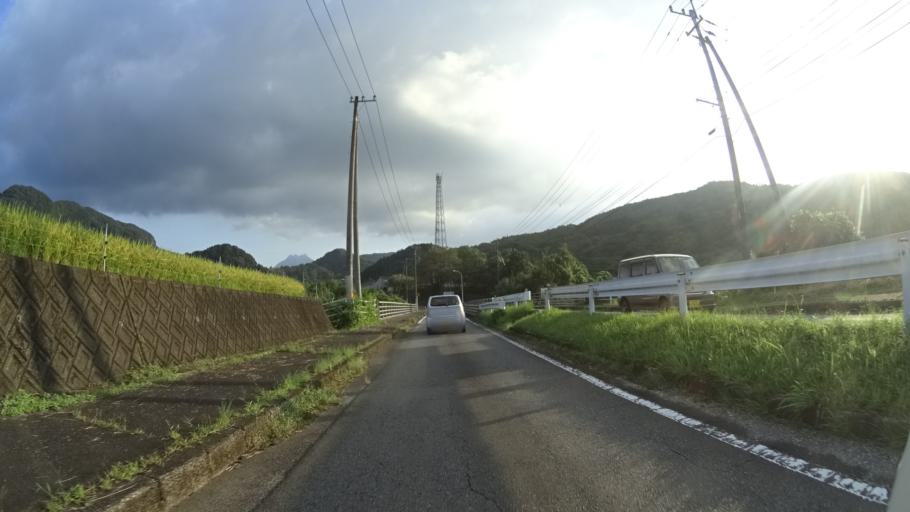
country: JP
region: Oita
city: Hiji
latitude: 33.3758
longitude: 131.3955
